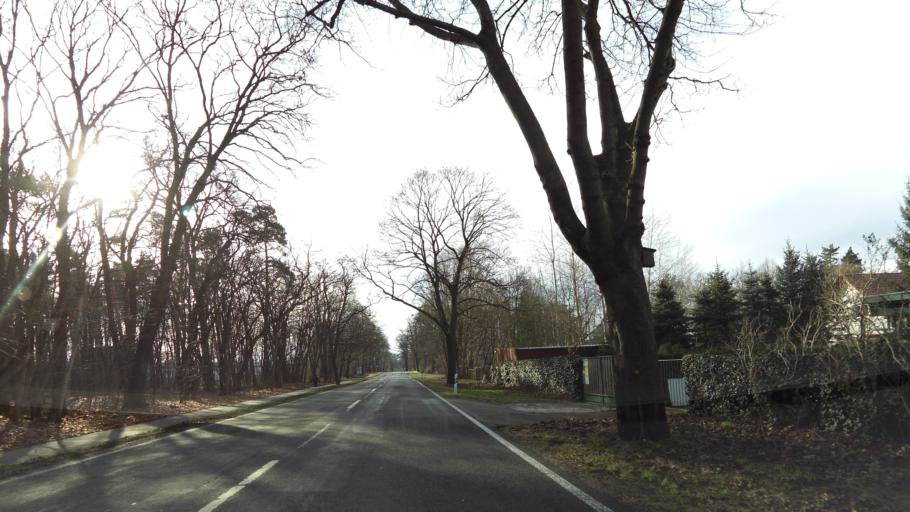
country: DE
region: Brandenburg
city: Michendorf
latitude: 52.3226
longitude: 13.0350
